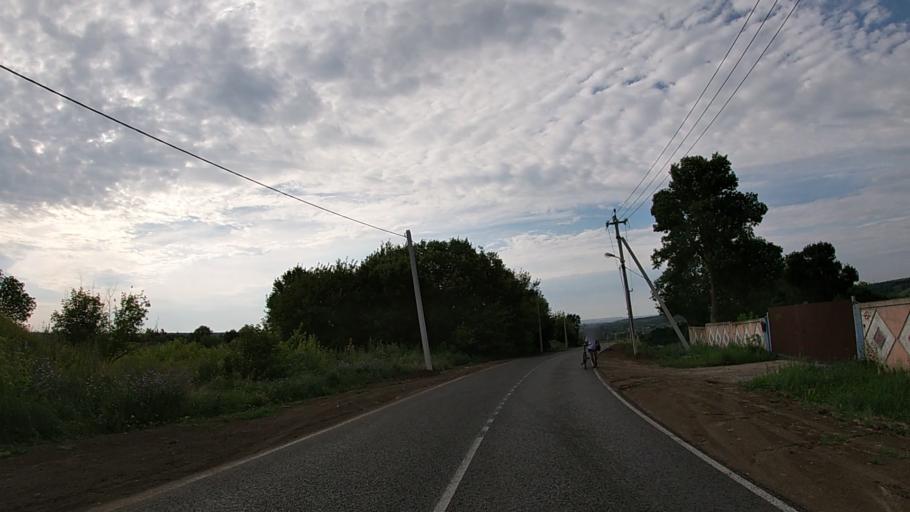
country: RU
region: Belgorod
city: Severnyy
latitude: 50.7186
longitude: 36.5882
